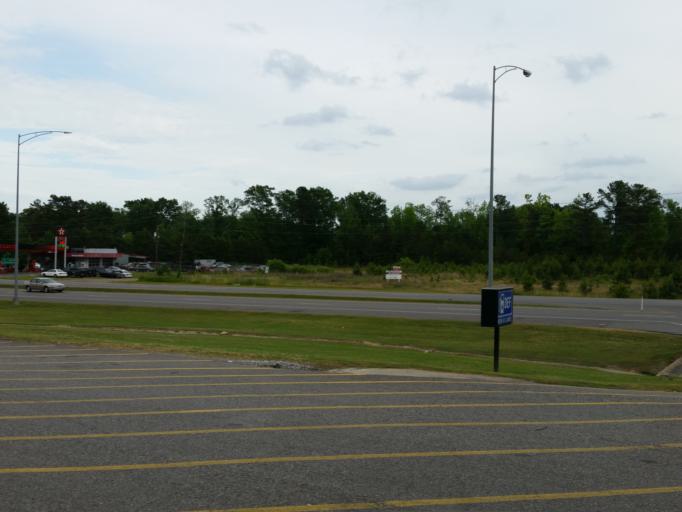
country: US
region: Alabama
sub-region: Tuscaloosa County
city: Holt
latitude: 33.1730
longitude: -87.4778
